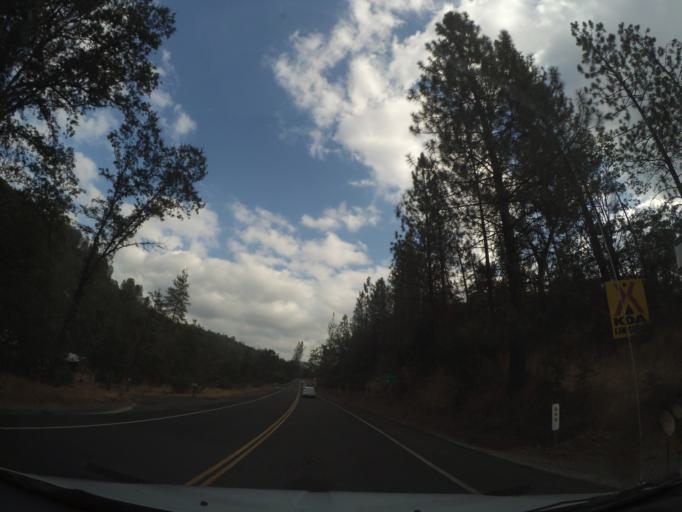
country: US
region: California
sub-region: Mariposa County
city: Midpines
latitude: 37.5441
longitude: -119.9201
